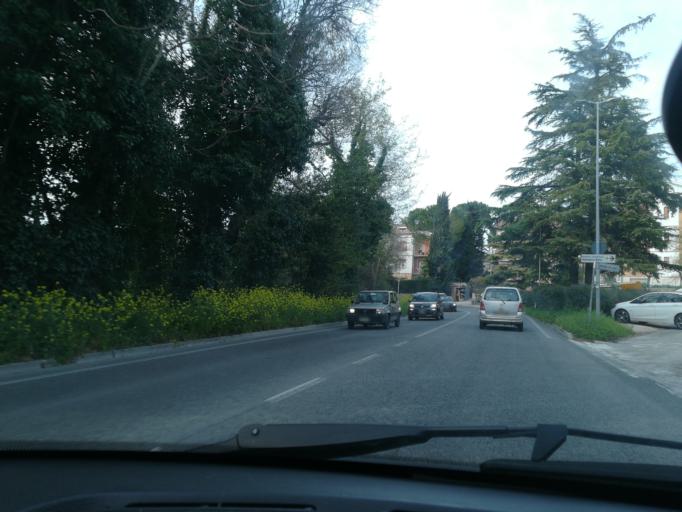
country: IT
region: The Marches
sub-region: Provincia di Macerata
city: Macerata
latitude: 43.2921
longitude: 13.4692
